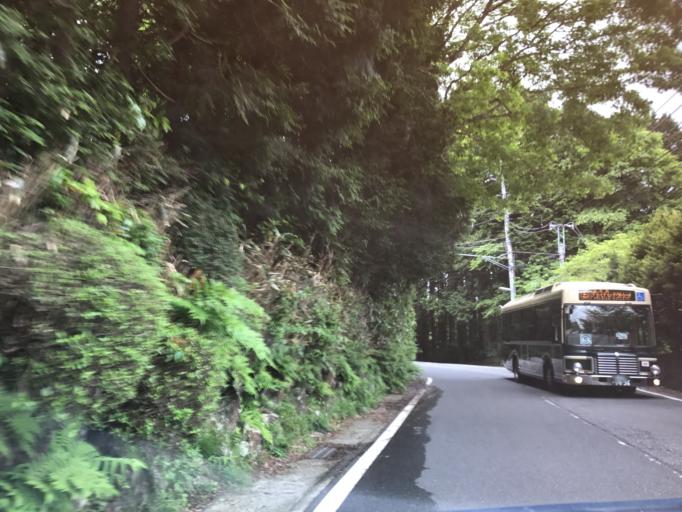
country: JP
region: Kanagawa
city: Hakone
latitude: 35.2640
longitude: 139.0139
